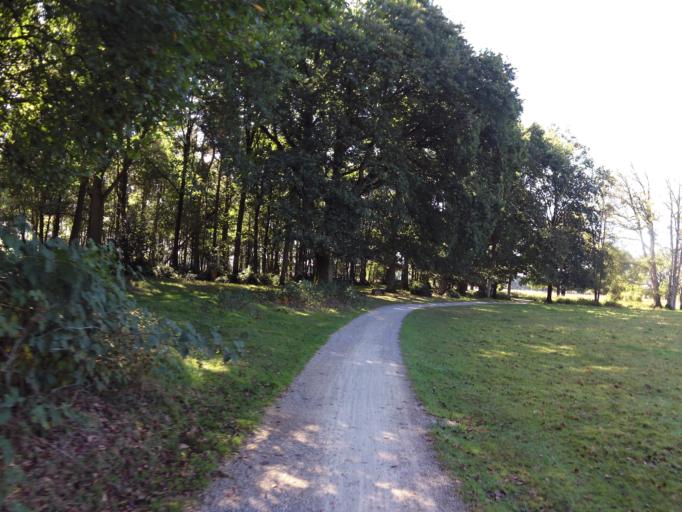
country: NL
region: Overijssel
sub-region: Gemeente Haaksbergen
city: Haaksbergen
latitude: 52.1613
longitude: 6.8018
